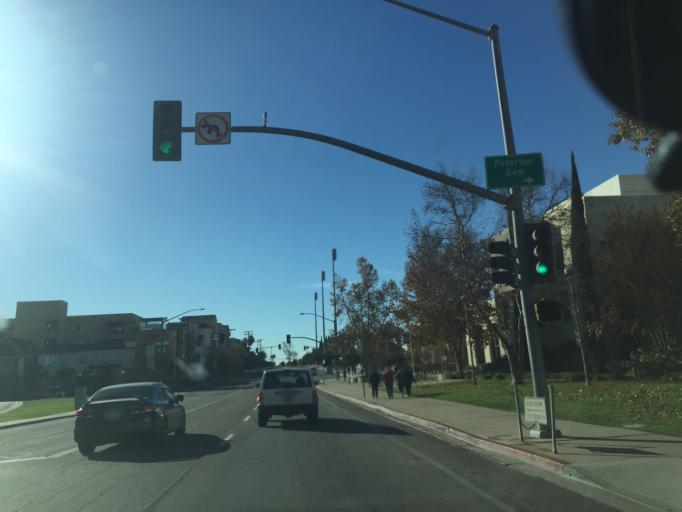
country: US
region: California
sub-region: San Diego County
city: La Mesa
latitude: 32.7740
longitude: -117.0762
